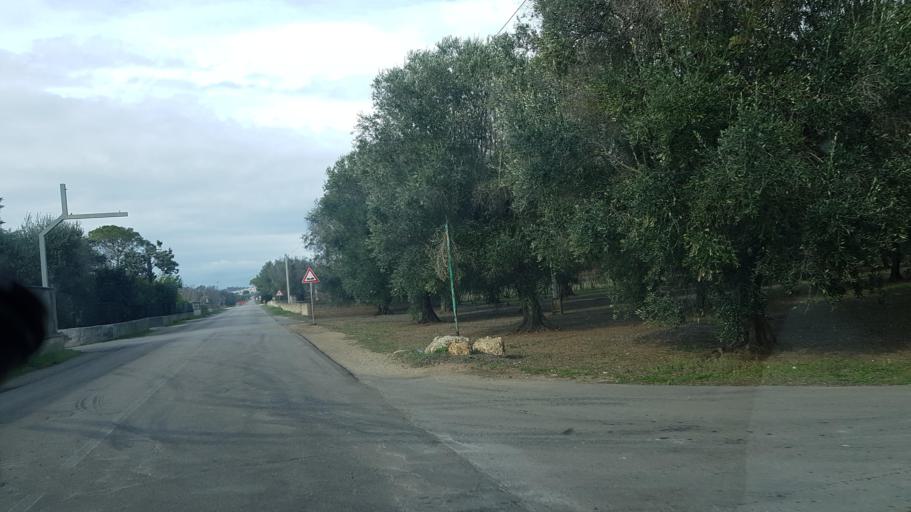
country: IT
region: Apulia
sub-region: Provincia di Brindisi
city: Oria
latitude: 40.4862
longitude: 17.6727
